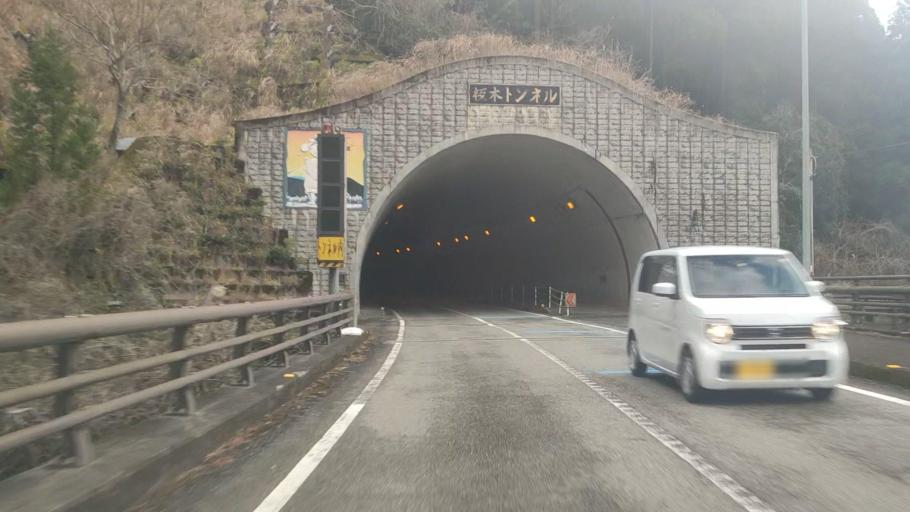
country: JP
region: Kumamoto
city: Hitoyoshi
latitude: 32.3936
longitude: 130.8273
